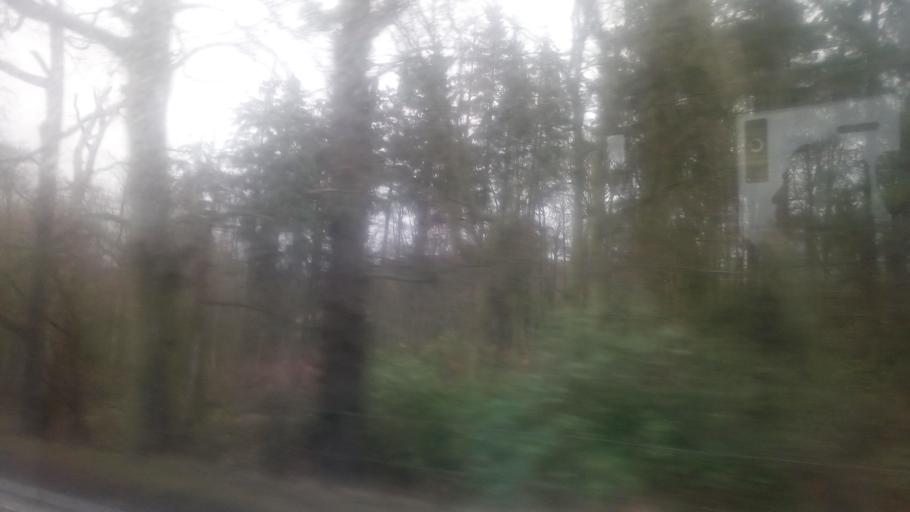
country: GB
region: Scotland
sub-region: The Scottish Borders
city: Newtown St Boswells
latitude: 55.5941
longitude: -2.6705
